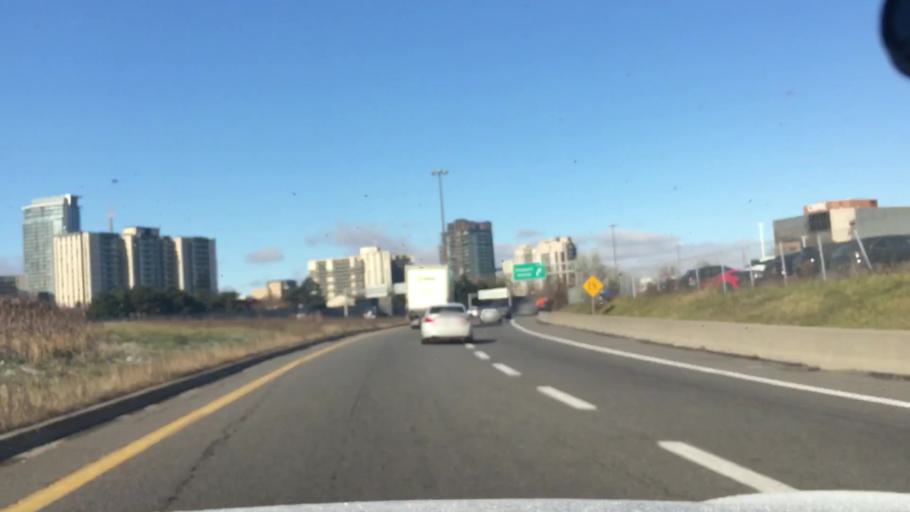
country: CA
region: Ontario
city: Willowdale
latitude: 43.7707
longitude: -79.3378
